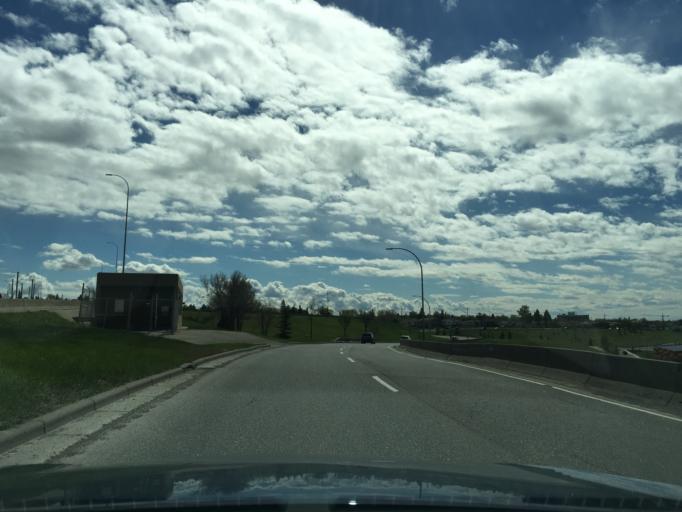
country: CA
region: Alberta
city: Calgary
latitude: 51.0452
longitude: -114.0066
